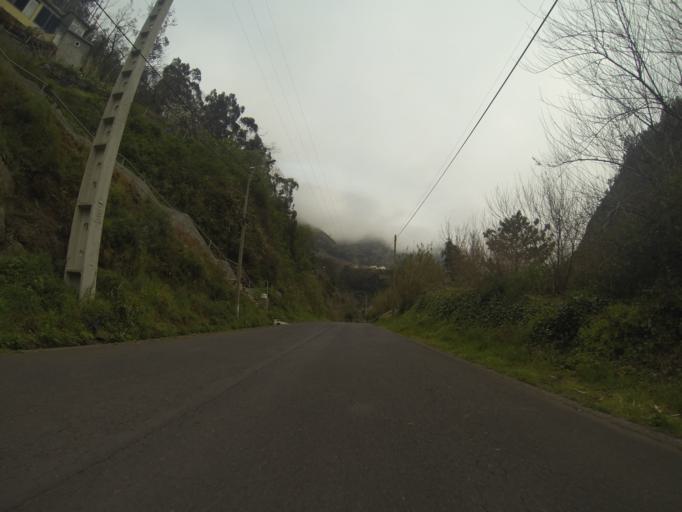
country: PT
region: Madeira
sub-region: Camara de Lobos
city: Curral das Freiras
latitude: 32.7255
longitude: -16.9660
